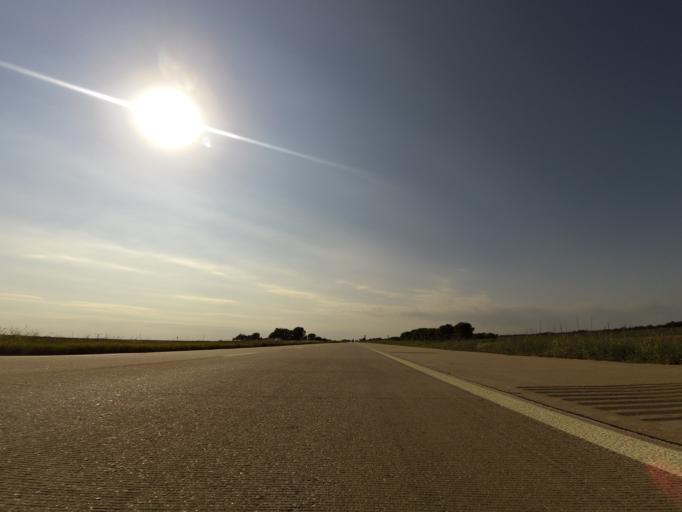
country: US
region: Kansas
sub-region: Sedgwick County
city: Colwich
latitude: 37.8454
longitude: -97.5859
